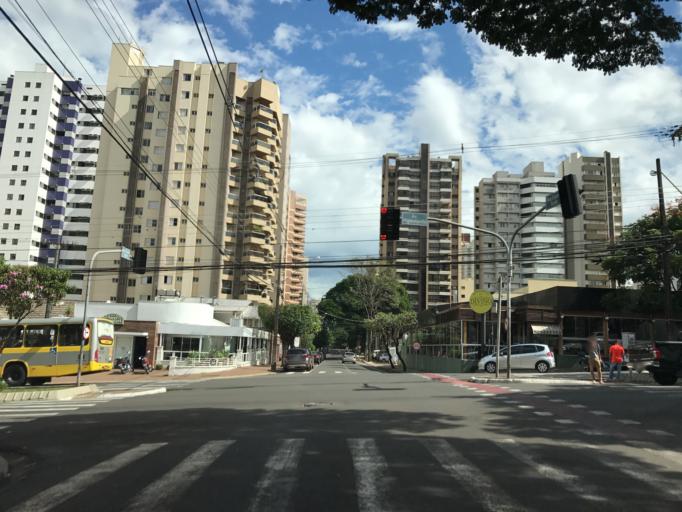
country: BR
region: Parana
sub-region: Londrina
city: Londrina
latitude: -23.3165
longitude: -51.1653
